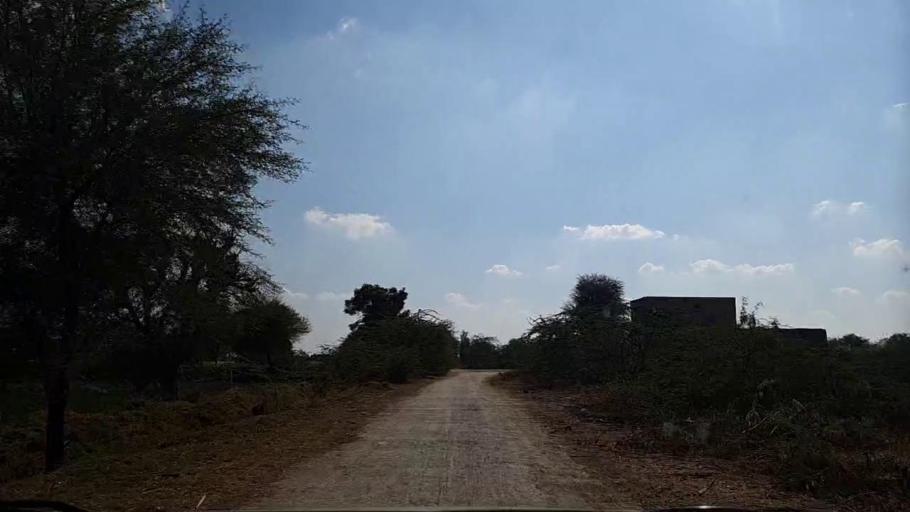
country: PK
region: Sindh
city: Pithoro
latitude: 25.6407
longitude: 69.4475
